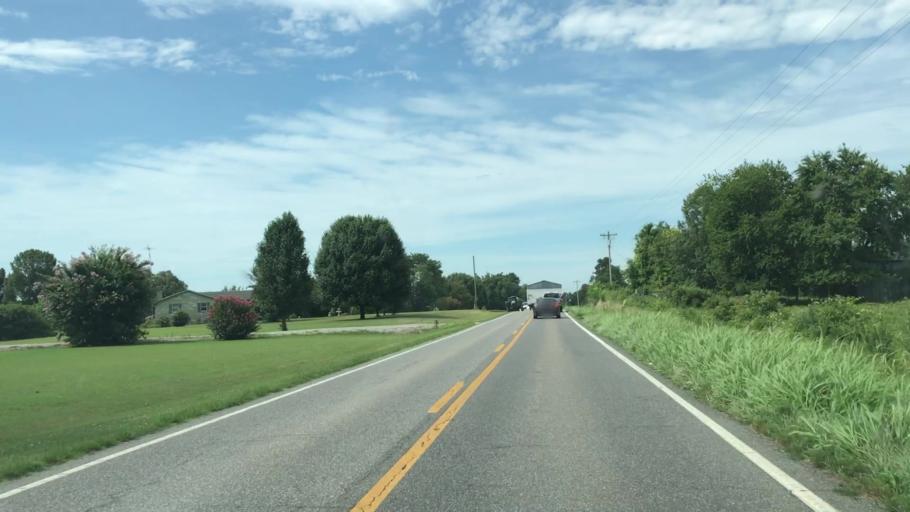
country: US
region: Kentucky
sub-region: Graves County
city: Mayfield
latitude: 36.8459
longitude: -88.5765
